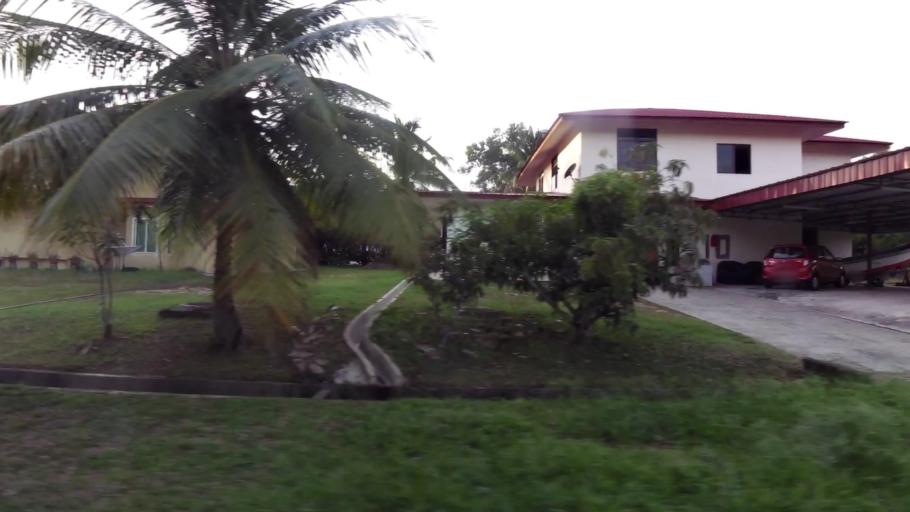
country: BN
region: Brunei and Muara
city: Bandar Seri Begawan
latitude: 4.9304
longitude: 114.8880
